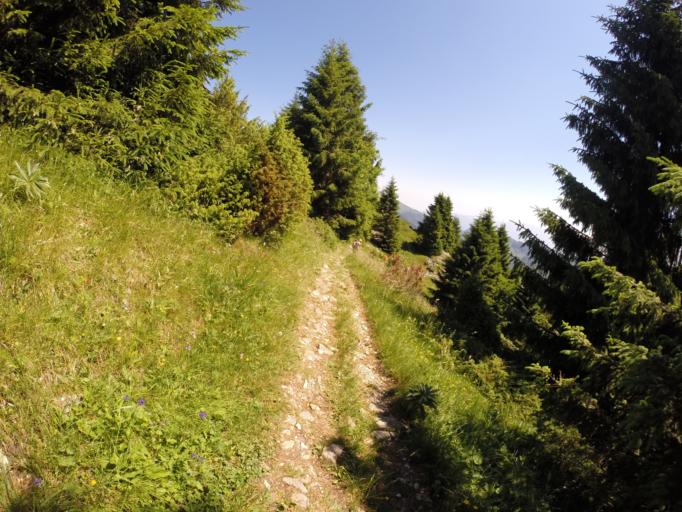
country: IT
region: Veneto
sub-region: Provincia di Treviso
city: Crespano del Grappa
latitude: 45.8918
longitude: 11.8128
